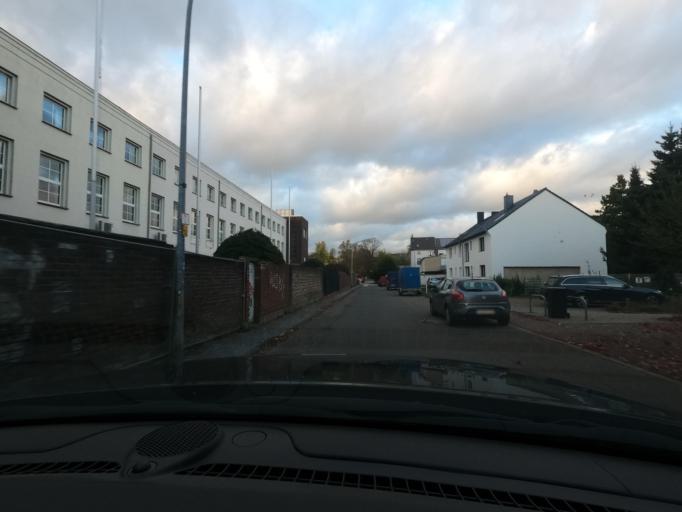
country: DE
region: North Rhine-Westphalia
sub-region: Regierungsbezirk Dusseldorf
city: Viersen
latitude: 51.2514
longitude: 6.3284
